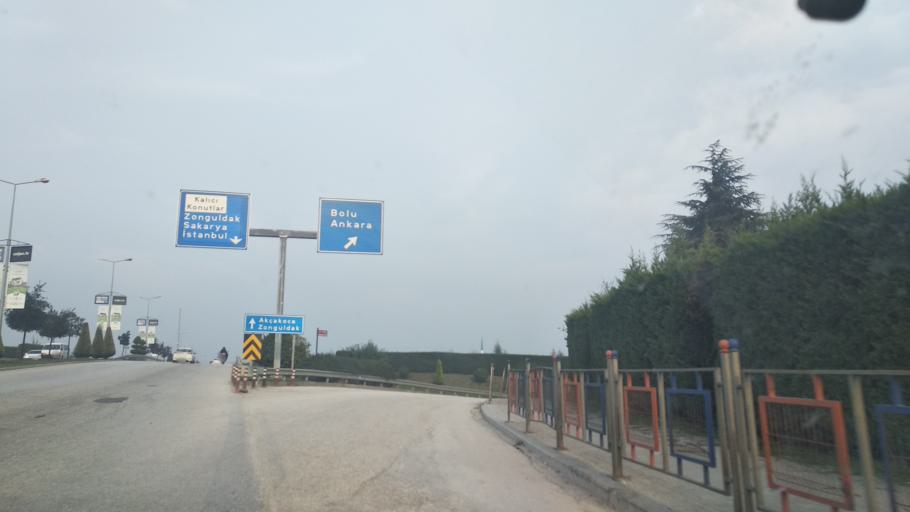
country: TR
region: Duzce
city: Duzce
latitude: 40.8363
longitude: 31.1721
